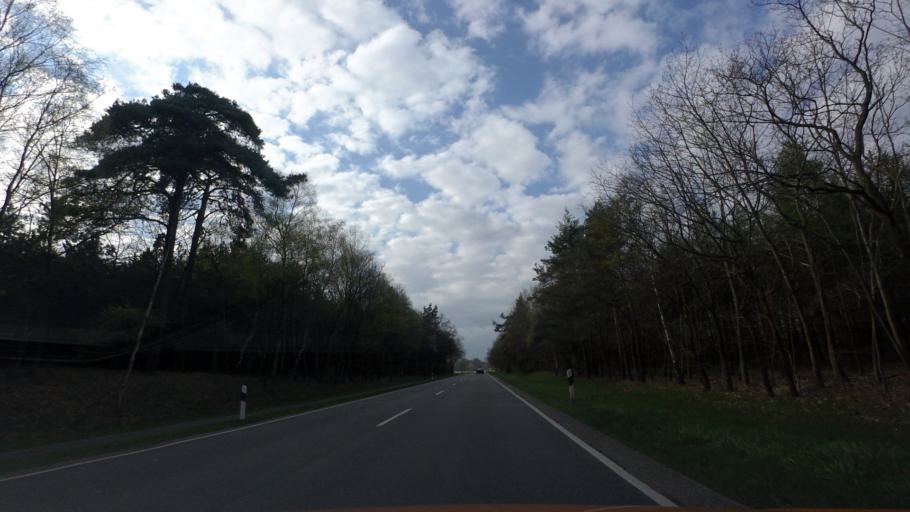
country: DE
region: Lower Saxony
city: Bosel
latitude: 52.9746
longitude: 7.9090
